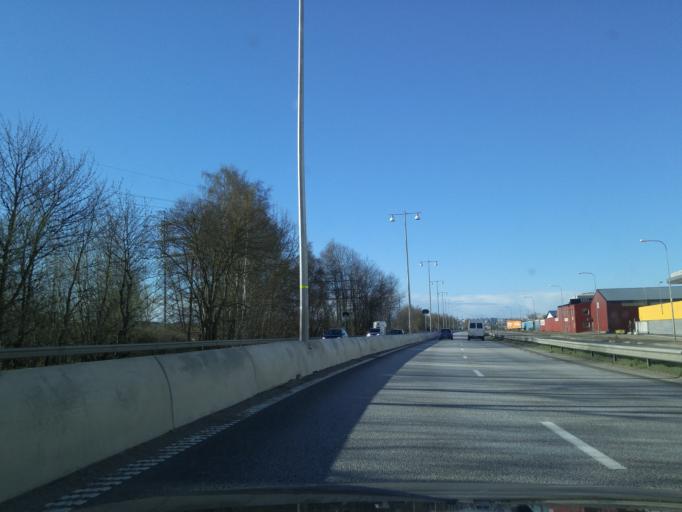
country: SE
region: Vaestra Goetaland
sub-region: Goteborg
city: Goeteborg
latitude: 57.7376
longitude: 12.0035
